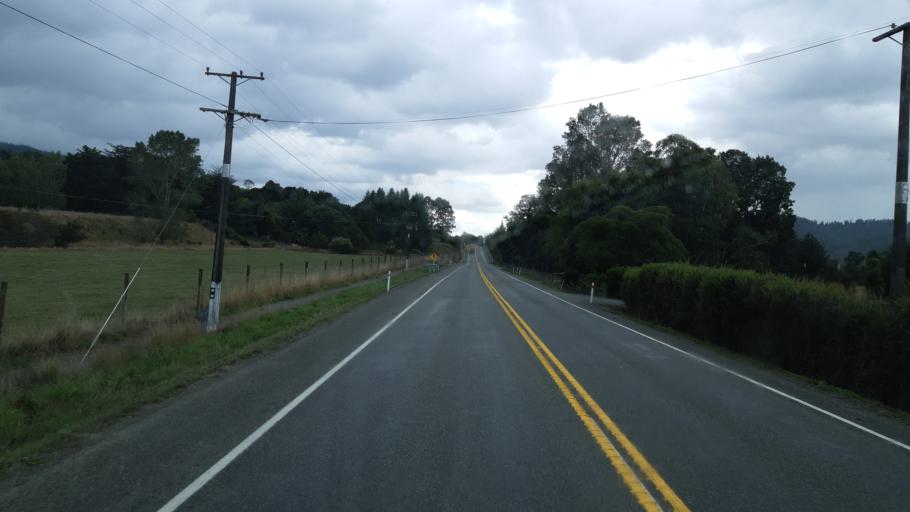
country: NZ
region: Tasman
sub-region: Tasman District
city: Wakefield
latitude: -41.4473
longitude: 172.9622
